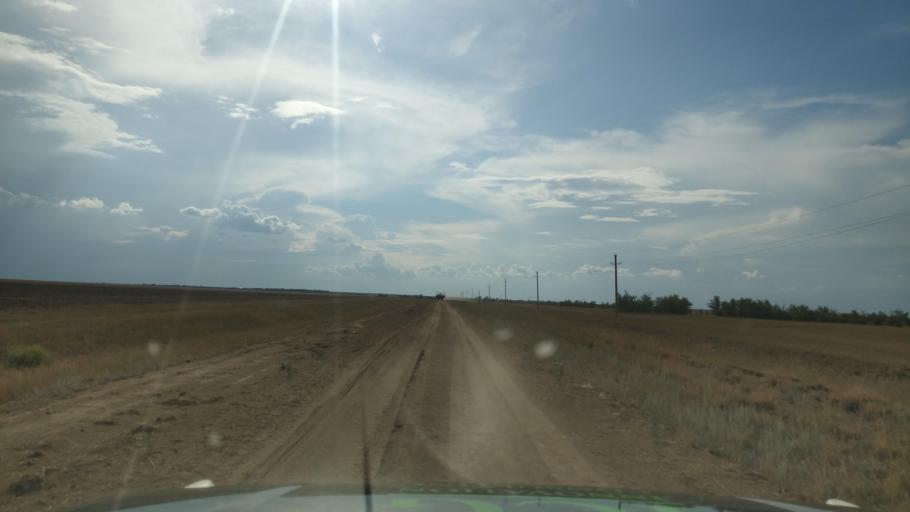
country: KZ
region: Pavlodar
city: Pavlodar
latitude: 52.5129
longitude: 77.4755
